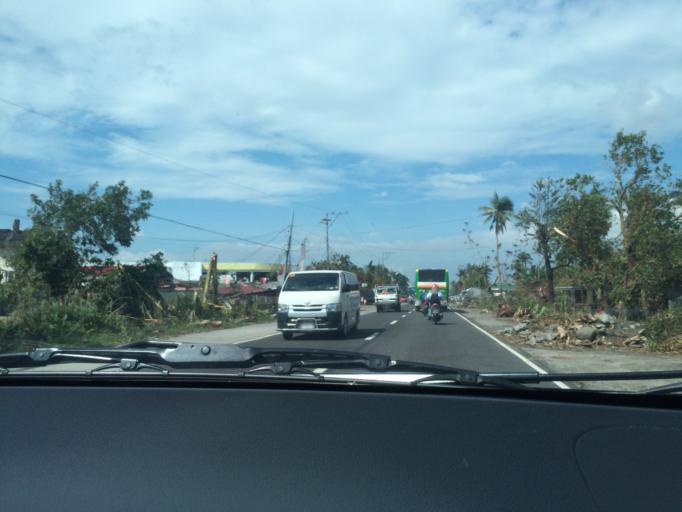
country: PH
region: Bicol
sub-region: Province of Albay
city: Iraya
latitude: 13.2595
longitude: 123.5009
